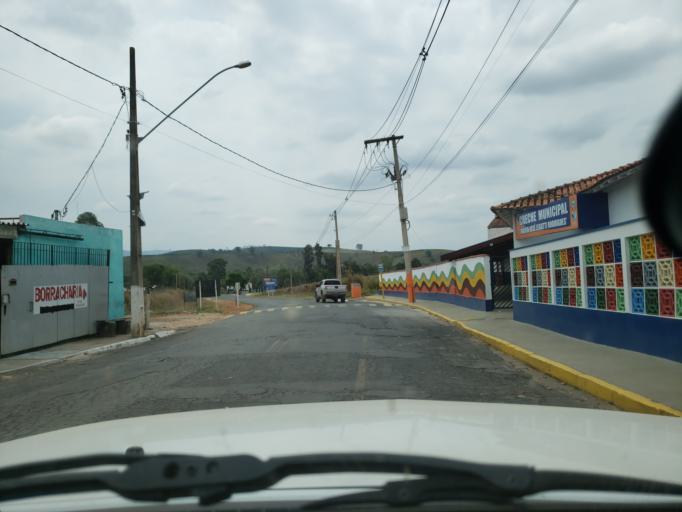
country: BR
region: Minas Gerais
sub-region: Jacutinga
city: Jacutinga
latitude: -22.2763
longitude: -46.6049
